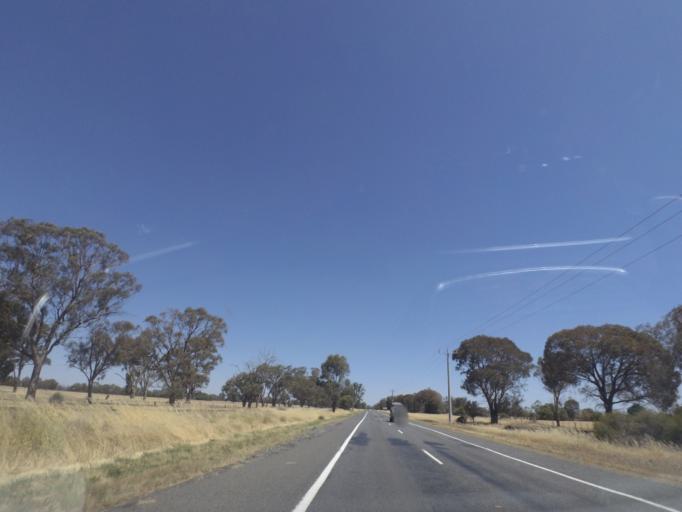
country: AU
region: Victoria
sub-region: Greater Shepparton
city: Shepparton
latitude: -36.2121
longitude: 145.4319
